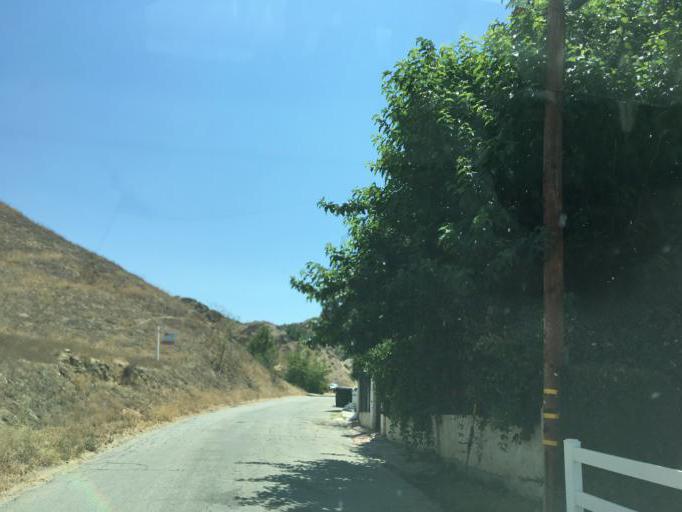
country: US
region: California
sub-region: Los Angeles County
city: Val Verde
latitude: 34.4459
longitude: -118.6557
